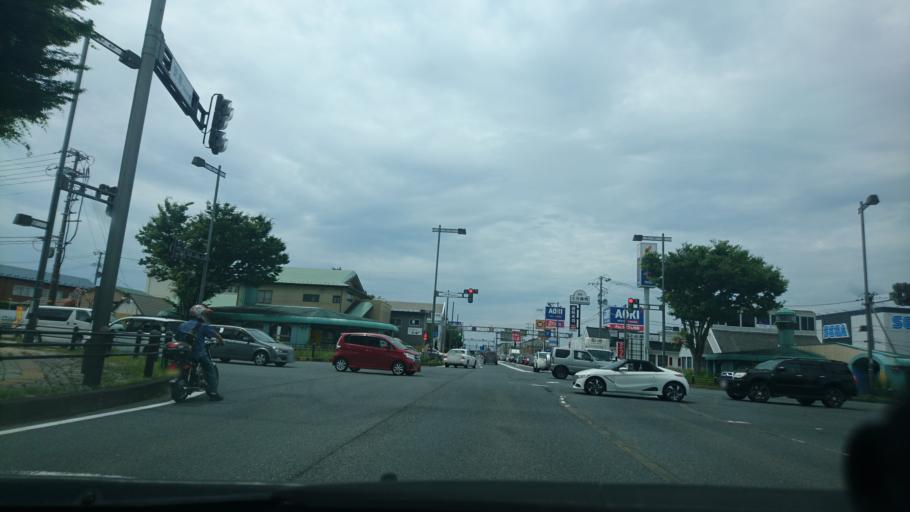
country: JP
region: Akita
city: Akita Shi
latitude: 39.7029
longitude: 140.1054
